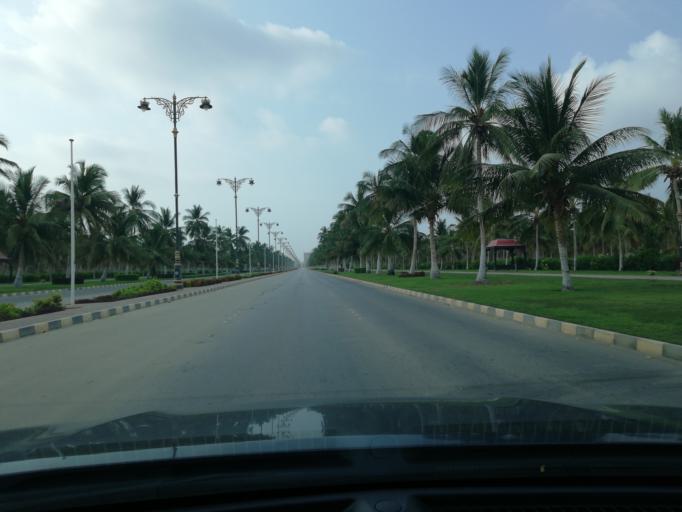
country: OM
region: Zufar
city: Salalah
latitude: 17.0362
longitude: 54.1074
